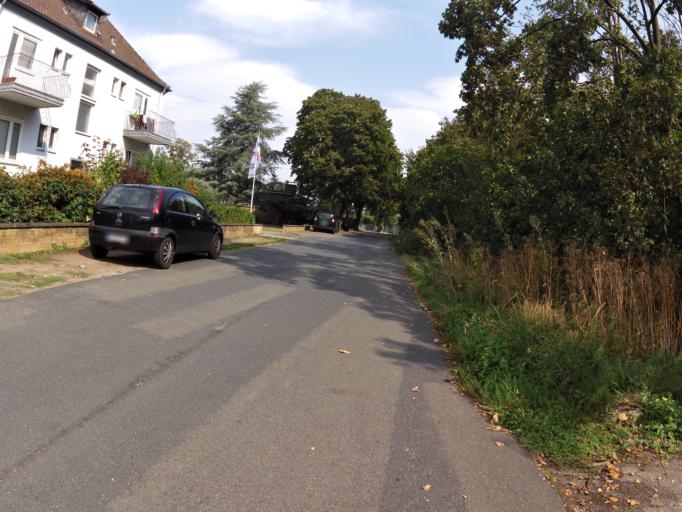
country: DE
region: Lower Saxony
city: Stolzenau
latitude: 52.5200
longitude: 9.0778
